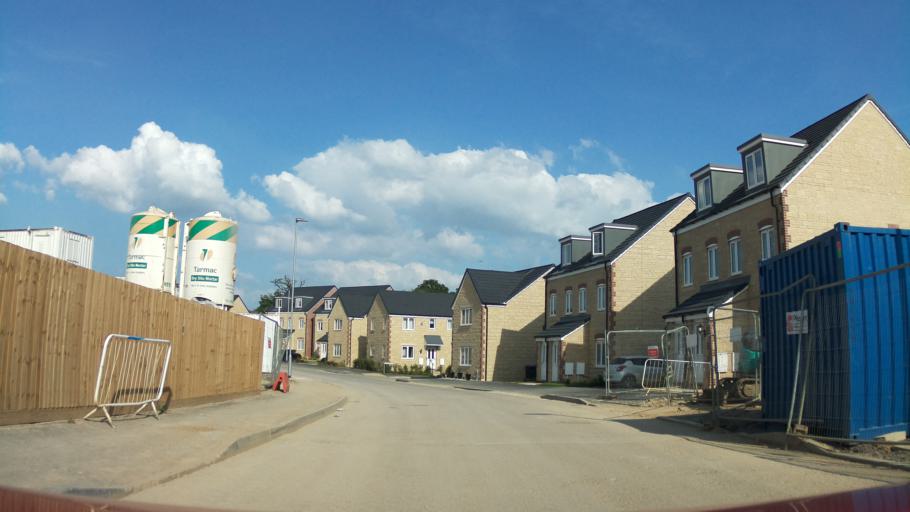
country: GB
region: England
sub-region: Wiltshire
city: Chippenham
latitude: 51.4736
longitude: -2.1177
